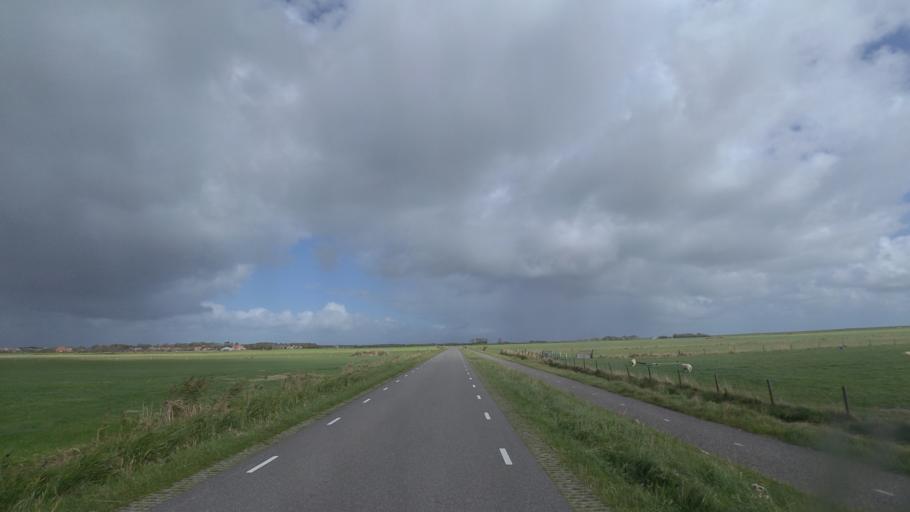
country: NL
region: Friesland
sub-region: Gemeente Ameland
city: Hollum
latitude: 53.4374
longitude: 5.6741
